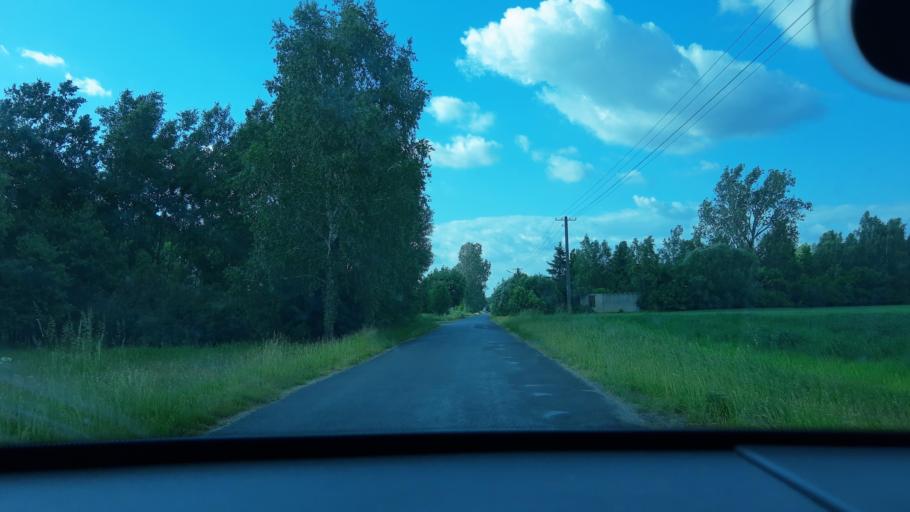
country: PL
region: Lodz Voivodeship
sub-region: Powiat zdunskowolski
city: Zapolice
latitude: 51.5195
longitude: 18.8441
